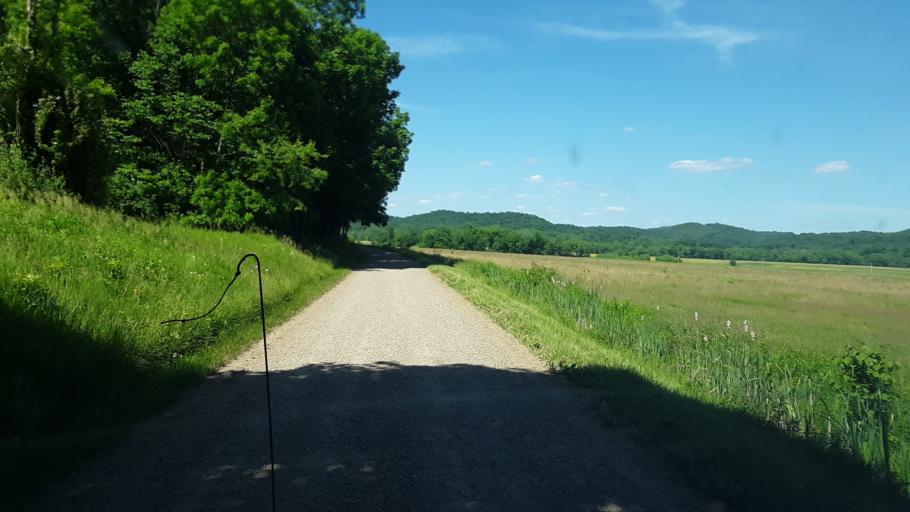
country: US
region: Ohio
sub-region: Coshocton County
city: West Lafayette
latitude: 40.2031
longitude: -81.6877
